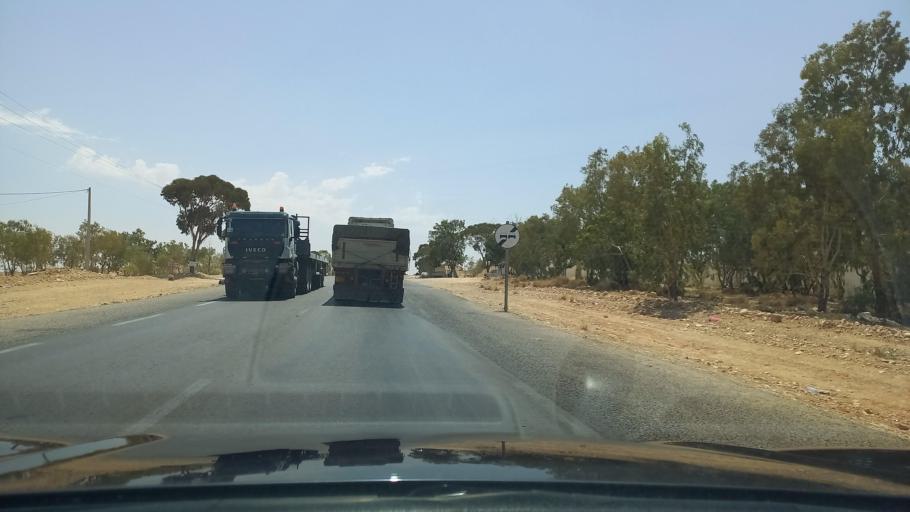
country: TN
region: Madanin
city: Medenine
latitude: 33.5748
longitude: 10.3171
